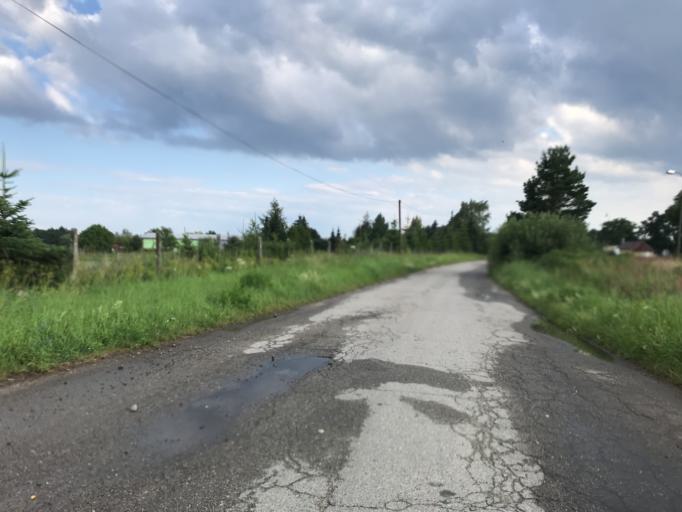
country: CZ
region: Jihocesky
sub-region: Okres Jindrichuv Hradec
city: Trebon
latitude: 49.0190
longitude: 14.7602
